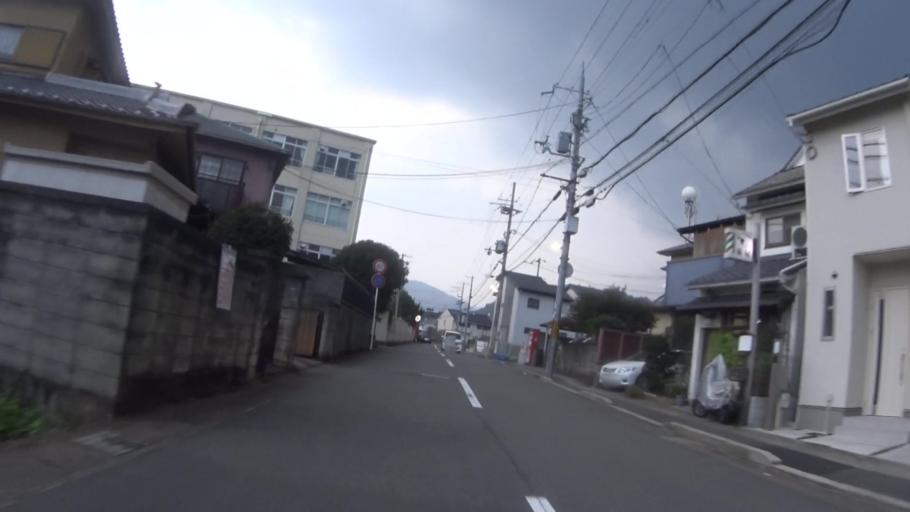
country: JP
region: Kyoto
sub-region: Kyoto-shi
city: Kamigyo-ku
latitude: 35.0688
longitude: 135.7462
